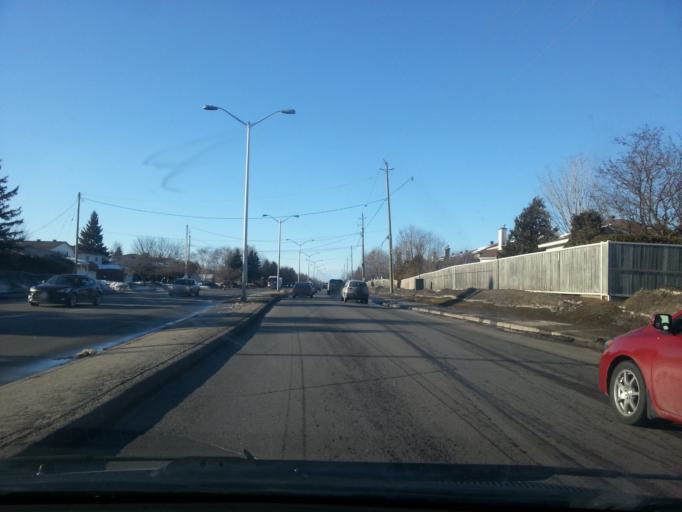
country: CA
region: Quebec
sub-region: Outaouais
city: Gatineau
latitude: 45.4616
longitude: -75.4881
